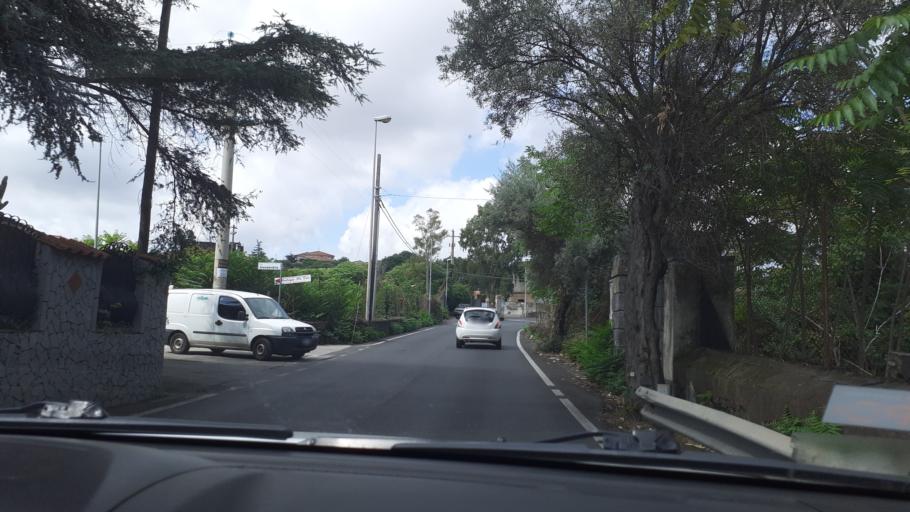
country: IT
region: Sicily
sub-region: Catania
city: San Giovanni la Punta
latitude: 37.5887
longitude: 15.0879
